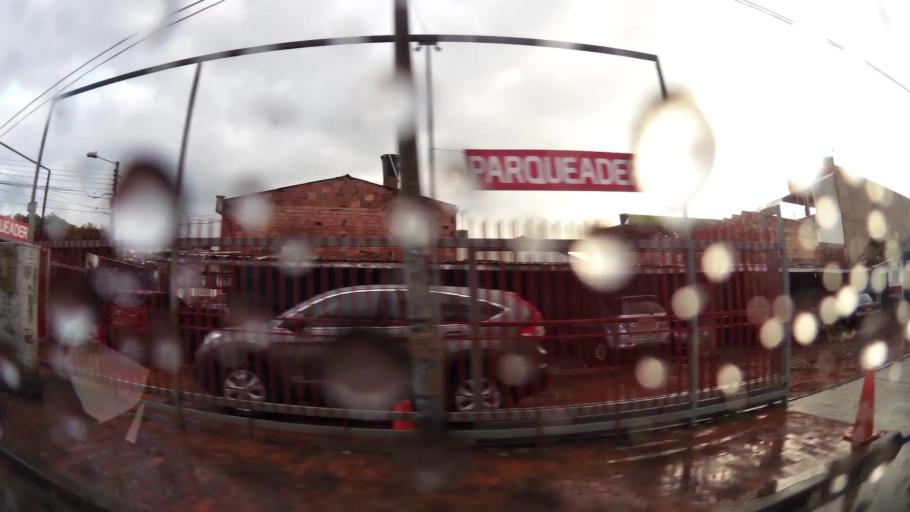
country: CO
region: Cundinamarca
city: Chia
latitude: 4.8590
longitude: -74.0600
